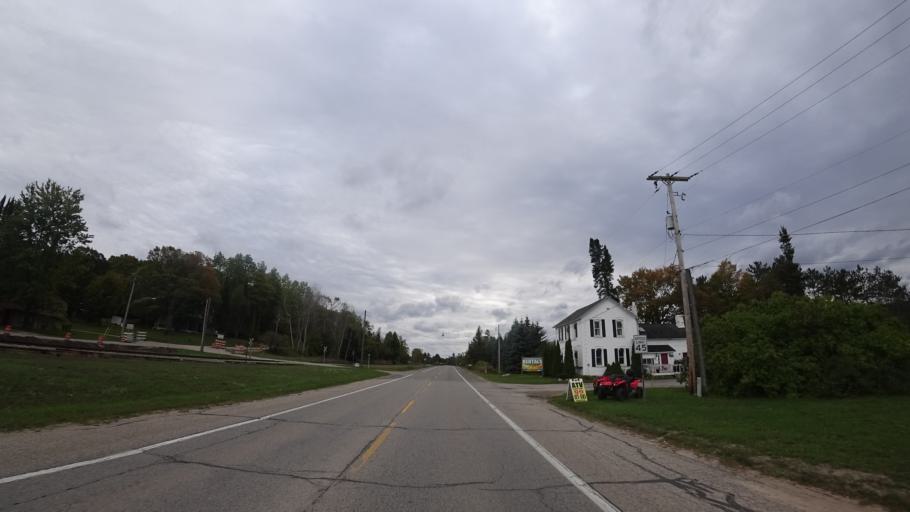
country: US
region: Michigan
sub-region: Charlevoix County
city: Boyne City
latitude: 45.1647
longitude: -84.9176
